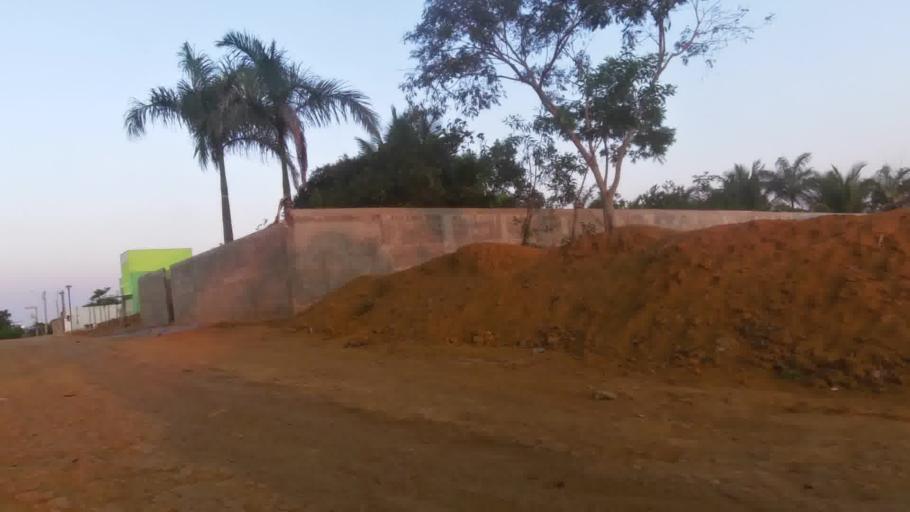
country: BR
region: Espirito Santo
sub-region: Piuma
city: Piuma
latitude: -20.8255
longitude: -40.7223
